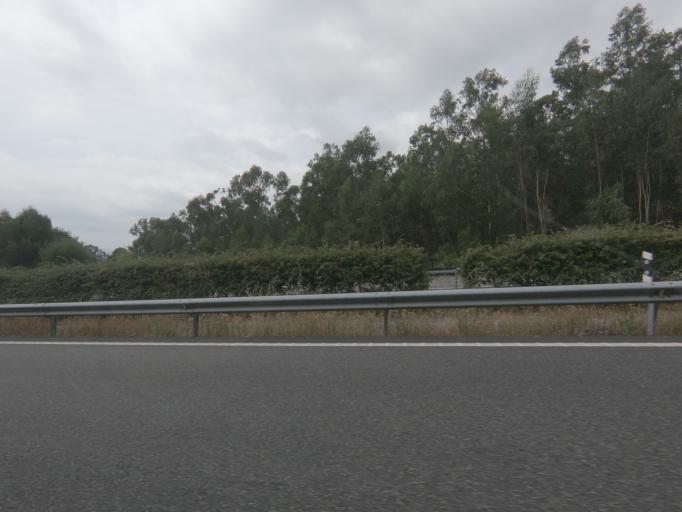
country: ES
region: Galicia
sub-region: Provincia de Pontevedra
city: Ponteareas
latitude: 42.1490
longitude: -8.4324
